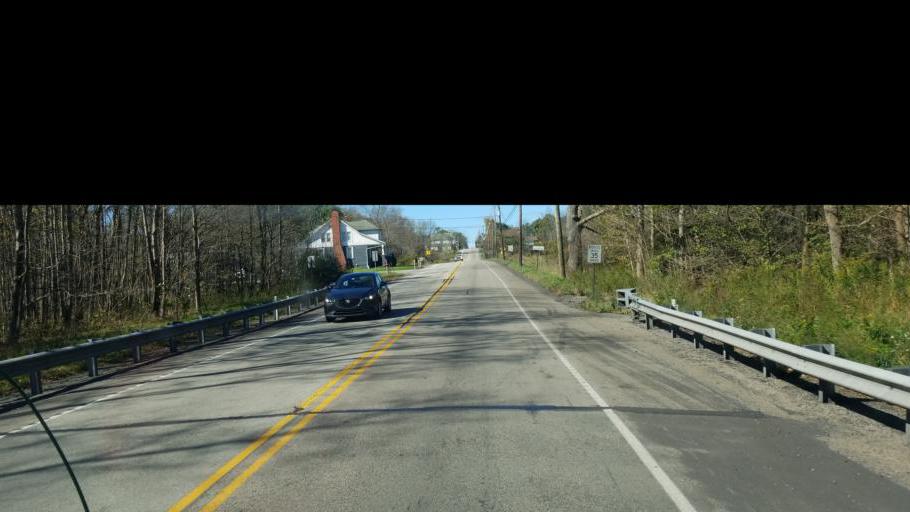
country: US
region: Pennsylvania
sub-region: Somerset County
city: Central City
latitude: 40.0698
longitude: -78.8575
